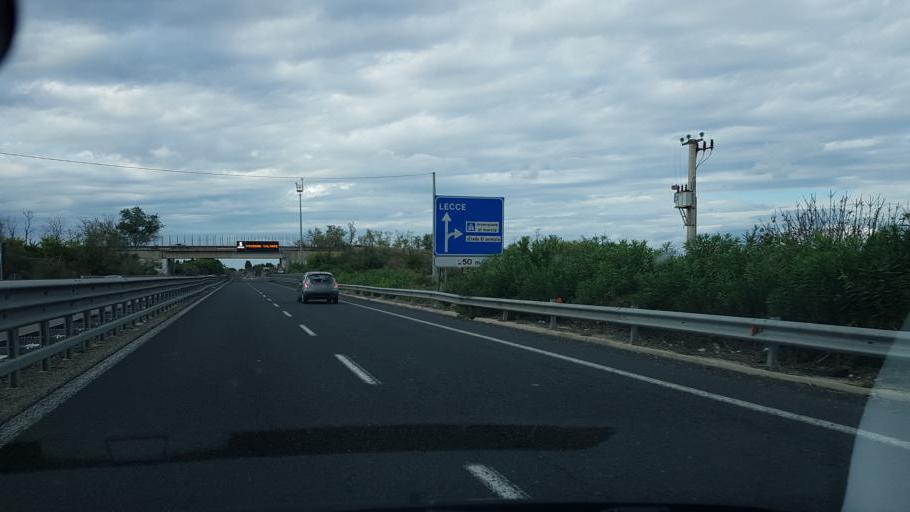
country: IT
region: Apulia
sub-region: Provincia di Lecce
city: Cavallino
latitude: 40.2980
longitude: 18.1945
